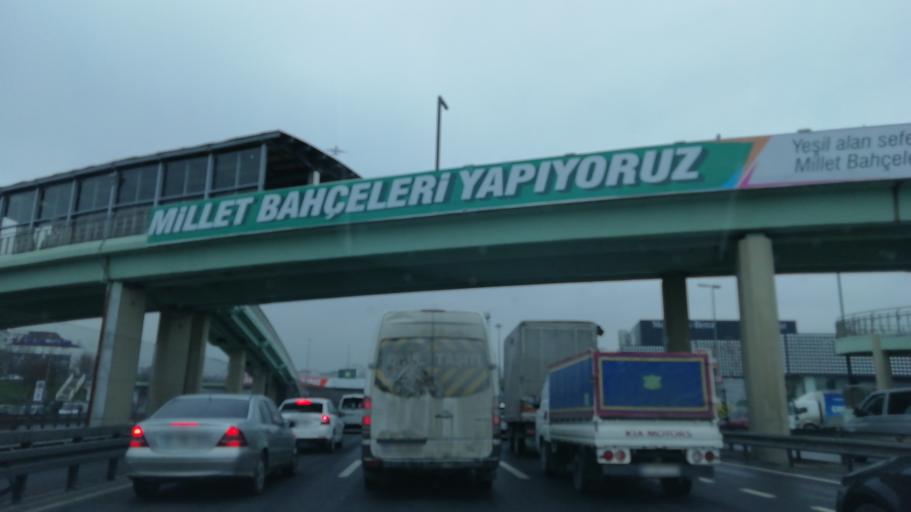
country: TR
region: Istanbul
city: guengoeren merter
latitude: 41.0026
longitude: 28.8893
